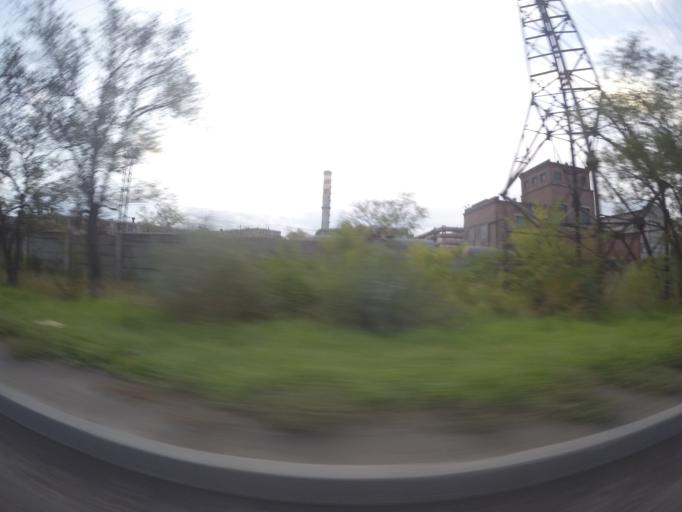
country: RU
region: Chelyabinsk
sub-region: Gorod Chelyabinsk
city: Chelyabinsk
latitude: 55.2003
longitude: 61.4370
